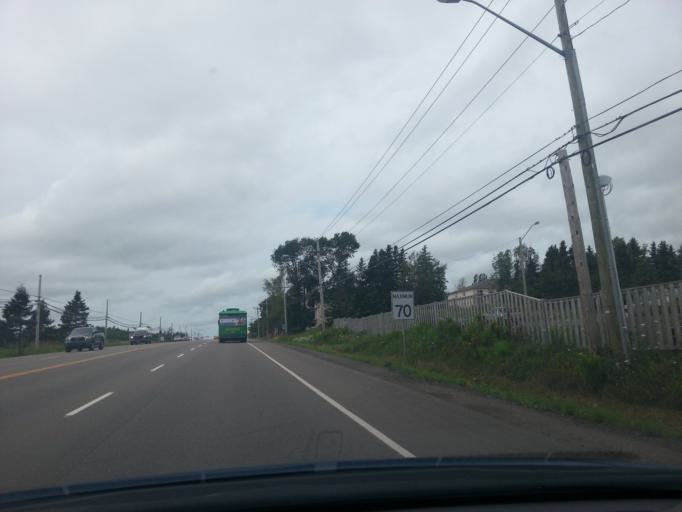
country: CA
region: Prince Edward Island
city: Charlottetown
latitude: 46.2631
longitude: -63.1643
